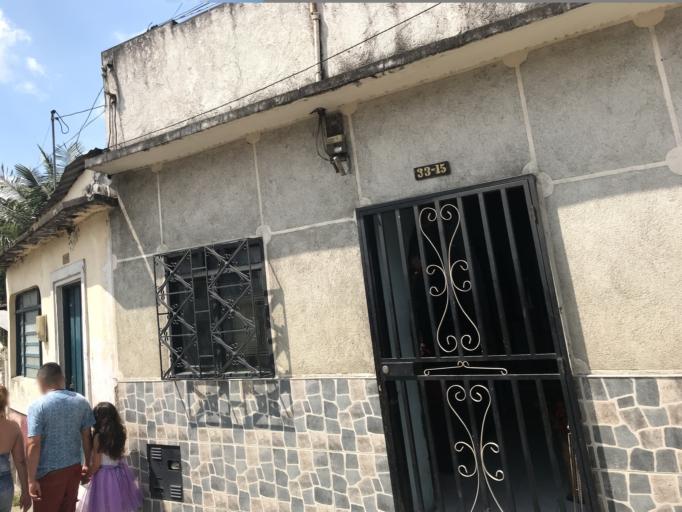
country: CO
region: Quindio
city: Calarca
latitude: 4.5249
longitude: -75.6373
